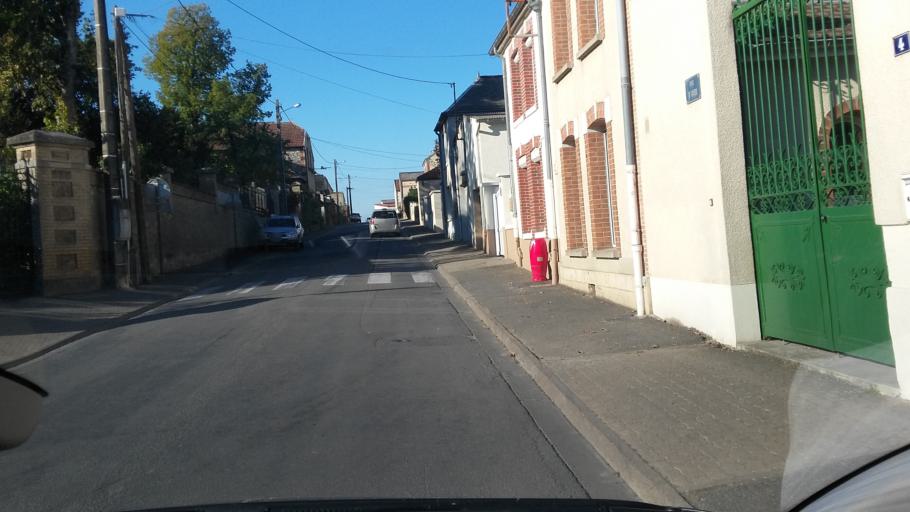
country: FR
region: Champagne-Ardenne
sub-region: Departement de la Marne
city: Le Mesnil-sur-Oger
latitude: 48.9488
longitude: 4.0247
